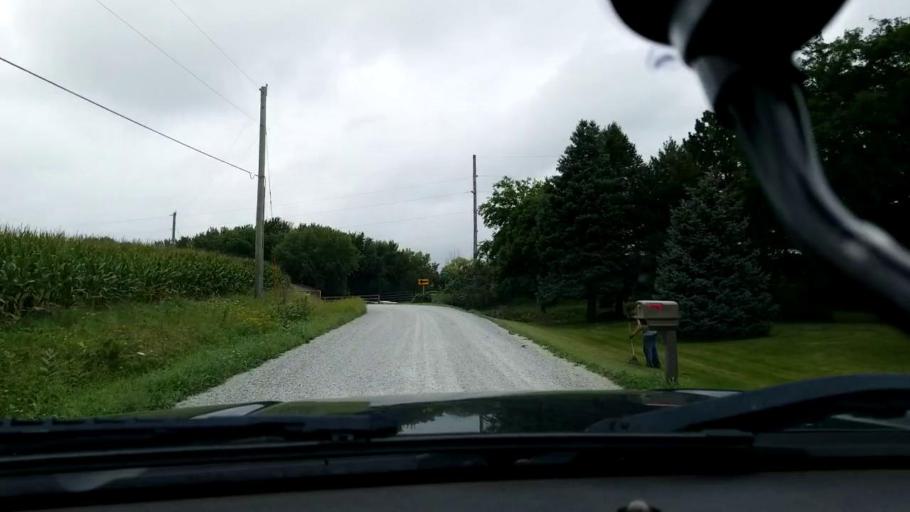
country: US
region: Iowa
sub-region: Buchanan County
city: Independence
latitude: 42.4898
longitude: -91.8837
